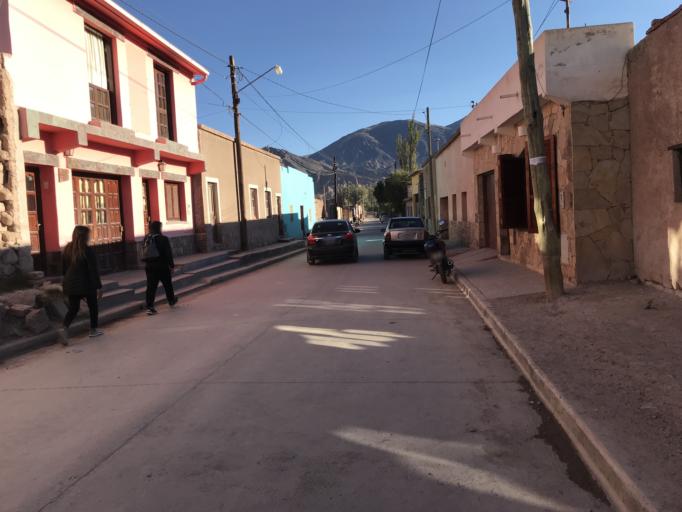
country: AR
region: Jujuy
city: Maimara
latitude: -23.5770
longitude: -65.3997
